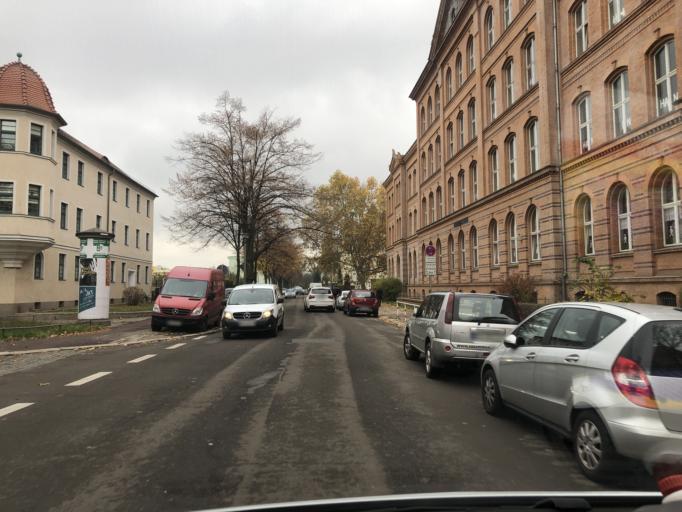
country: DE
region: Saxony-Anhalt
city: Halle (Saale)
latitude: 51.4703
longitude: 11.9739
